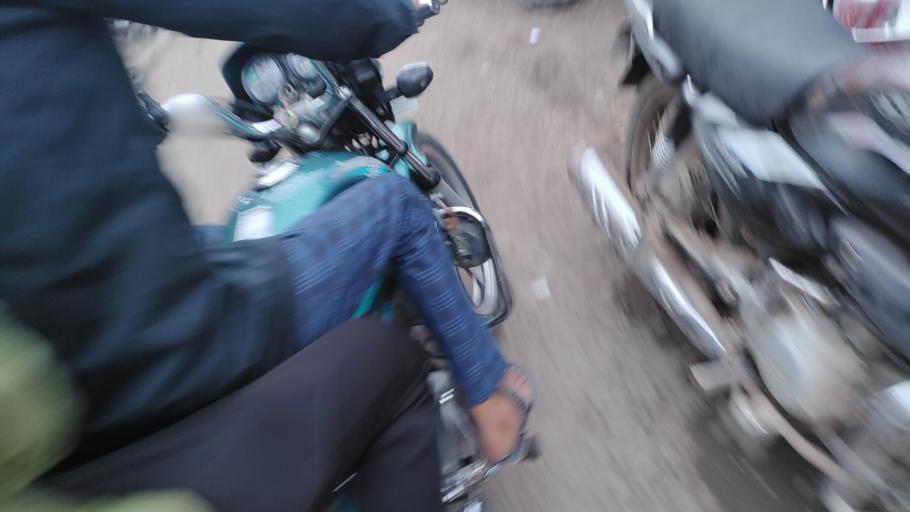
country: IN
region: Maharashtra
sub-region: Aurangabad Division
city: Aurangabad
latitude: 19.8857
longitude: 75.3286
